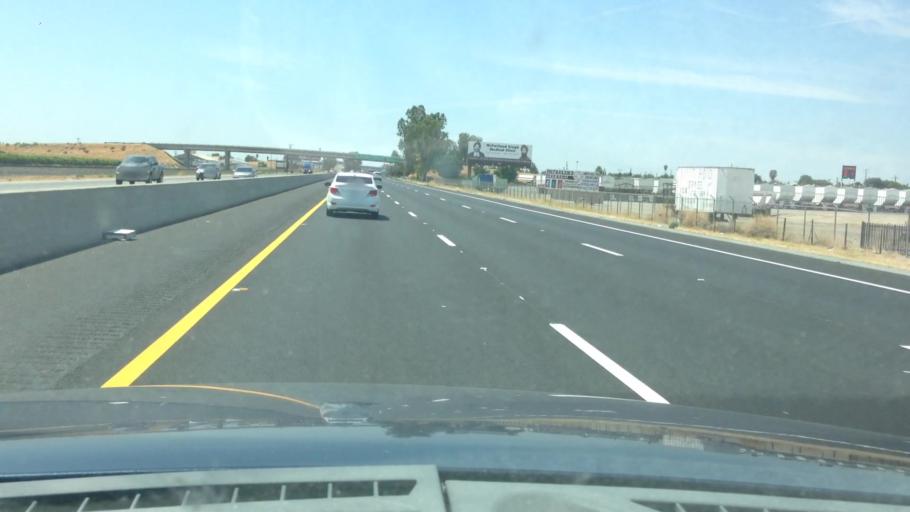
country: US
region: California
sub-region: Kern County
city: McFarland
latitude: 35.6929
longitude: -119.2307
